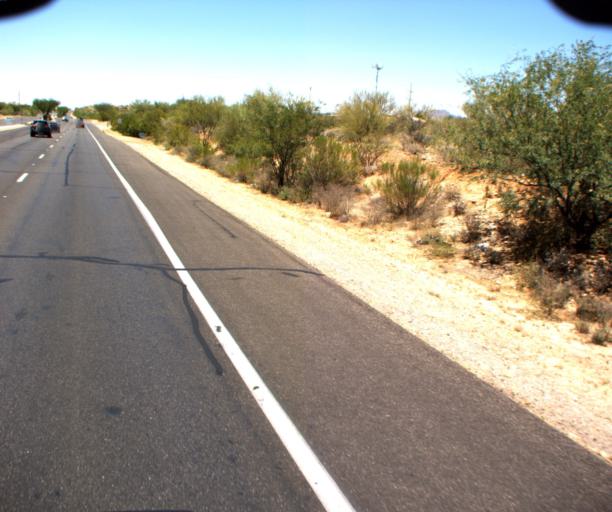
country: US
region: Arizona
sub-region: Pima County
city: Oro Valley
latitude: 32.4241
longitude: -110.9670
